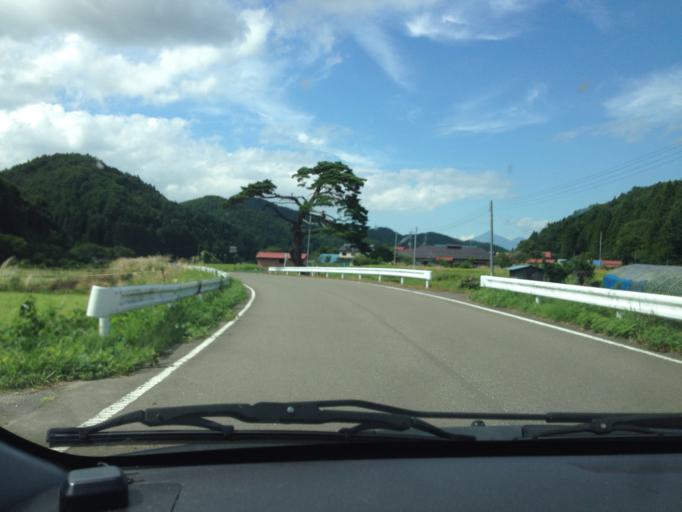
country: JP
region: Fukushima
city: Inawashiro
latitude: 37.3627
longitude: 140.0833
